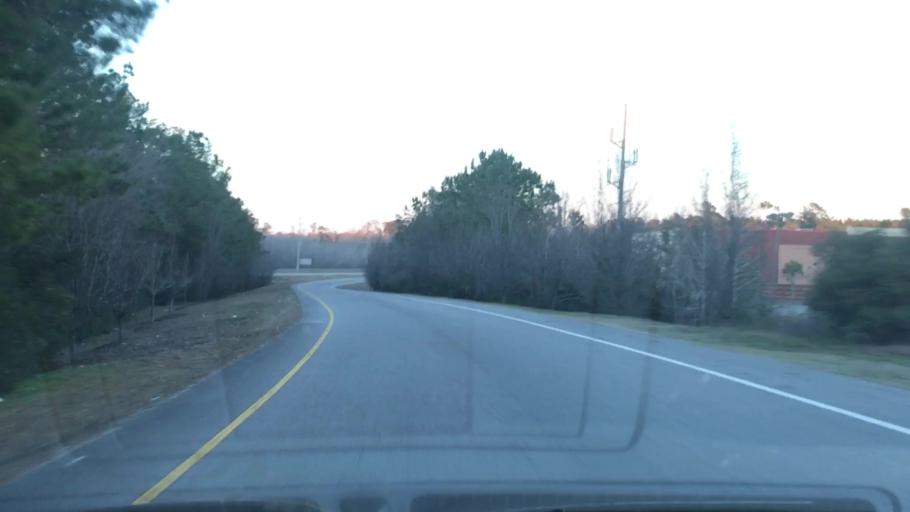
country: US
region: North Carolina
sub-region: Brunswick County
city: Shallotte
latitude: 33.9766
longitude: -78.4022
